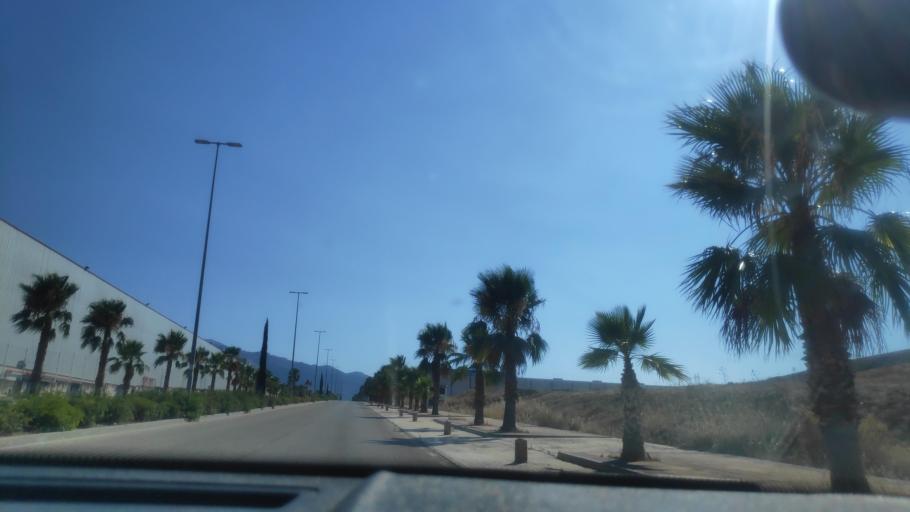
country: ES
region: Andalusia
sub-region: Provincia de Jaen
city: Jaen
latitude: 37.8192
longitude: -3.7789
